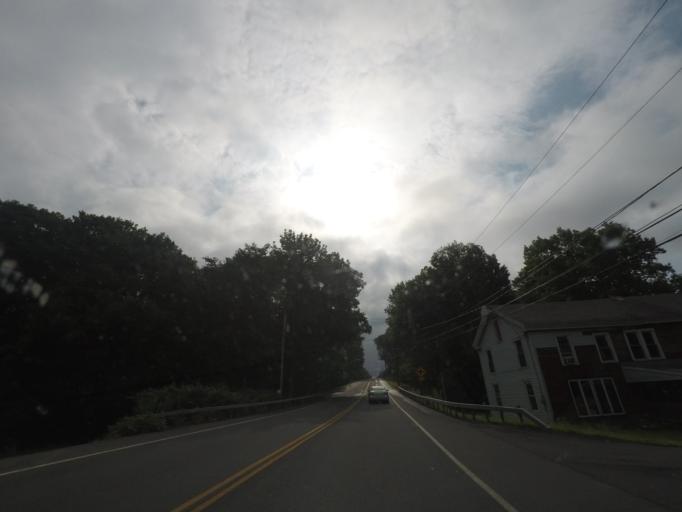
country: US
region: New York
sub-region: Rensselaer County
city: Nassau
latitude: 42.4973
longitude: -73.5291
